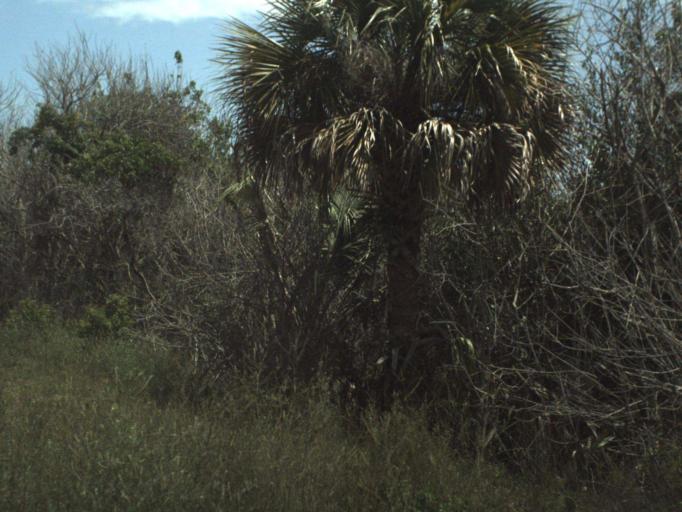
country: US
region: Florida
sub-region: Brevard County
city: Merritt Island
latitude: 28.6435
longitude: -80.6425
